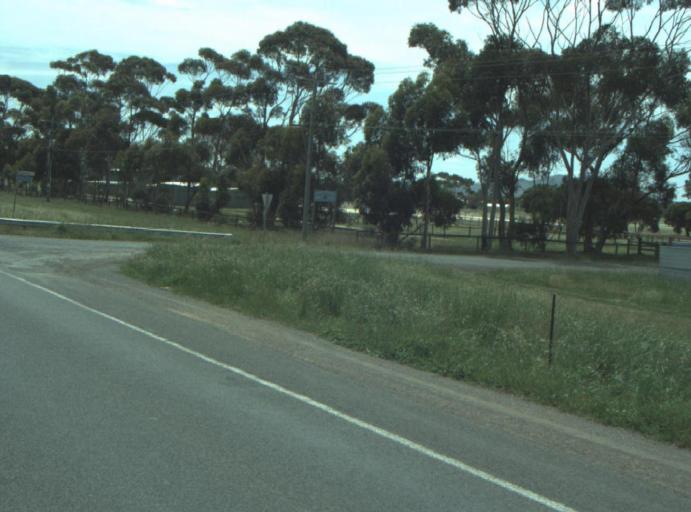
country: AU
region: Victoria
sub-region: Greater Geelong
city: Lara
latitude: -38.0334
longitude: 144.3550
